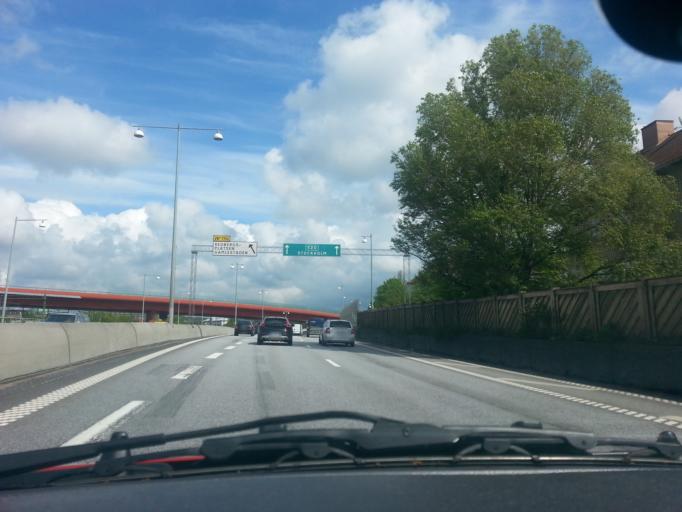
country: SE
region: Vaestra Goetaland
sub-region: Goteborg
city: Goeteborg
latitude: 57.7219
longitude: 12.0051
